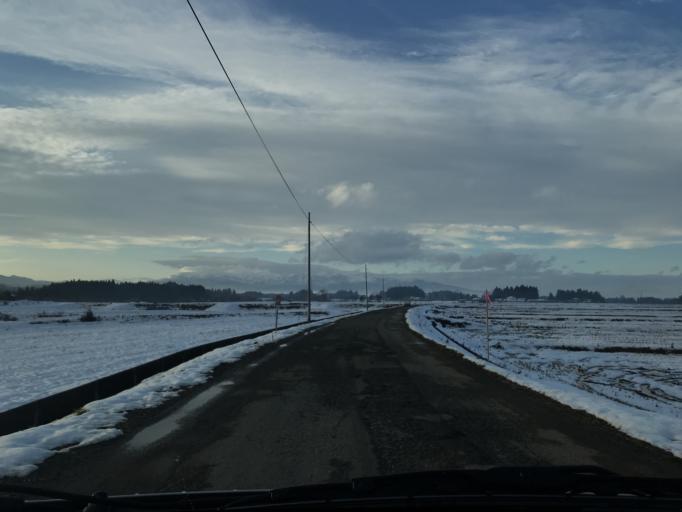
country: JP
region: Iwate
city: Mizusawa
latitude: 39.0565
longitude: 141.0921
